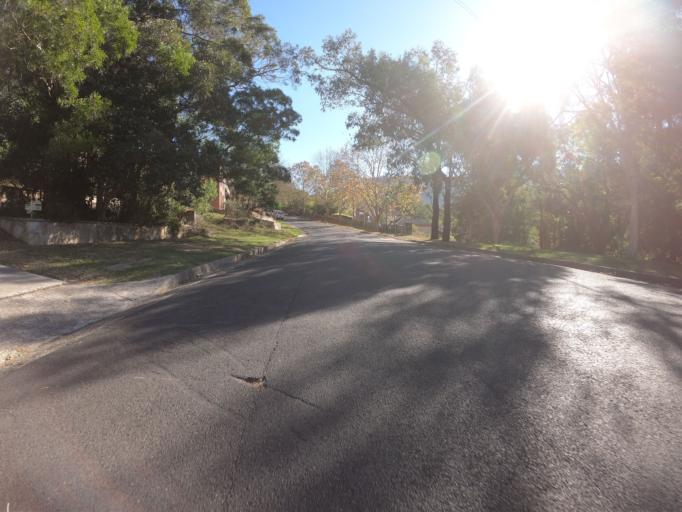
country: AU
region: New South Wales
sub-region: Wollongong
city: Mount Keira
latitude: -34.4174
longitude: 150.8523
